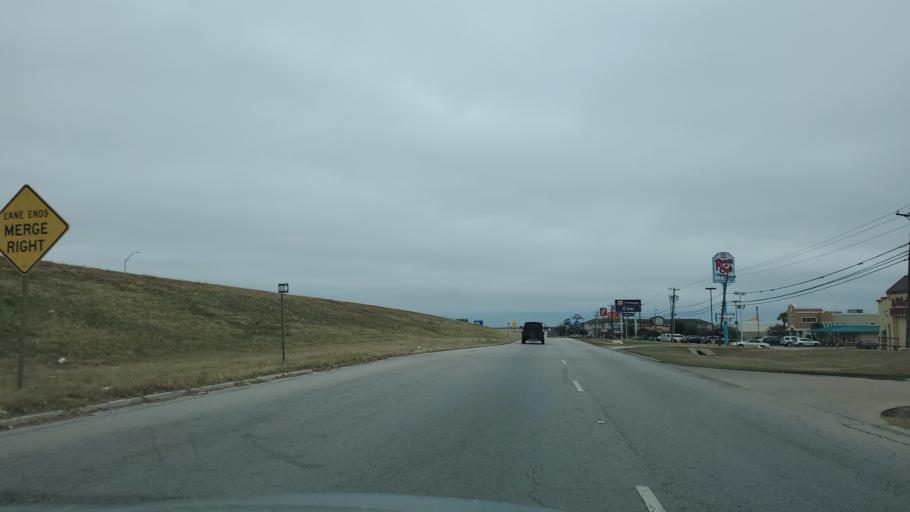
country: US
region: Texas
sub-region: Bell County
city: Killeen
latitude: 31.0940
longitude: -97.7319
